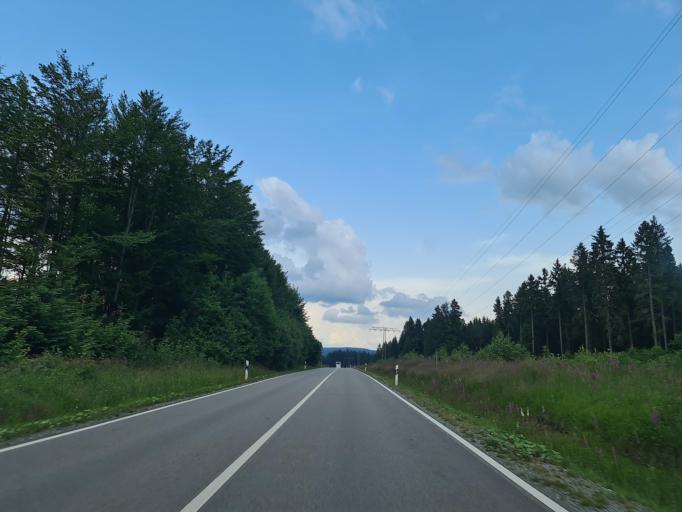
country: DE
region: Saxony
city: Grunbach
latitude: 50.4278
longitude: 12.3742
